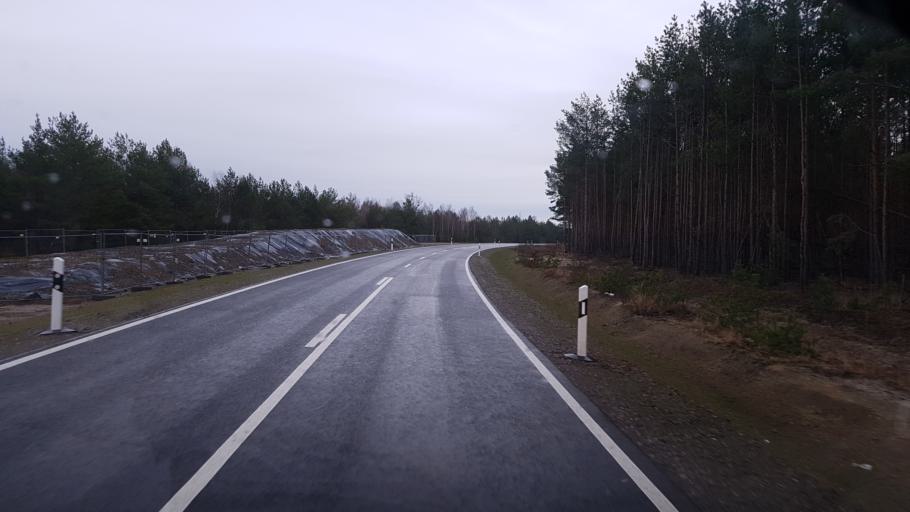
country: DE
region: Brandenburg
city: Lauchhammer
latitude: 51.5224
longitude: 13.7917
